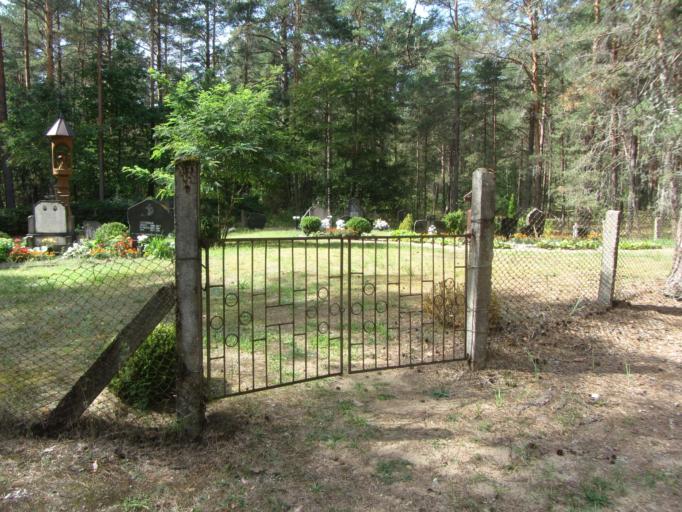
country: LT
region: Alytaus apskritis
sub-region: Alytaus rajonas
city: Daugai
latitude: 54.1343
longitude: 24.2586
